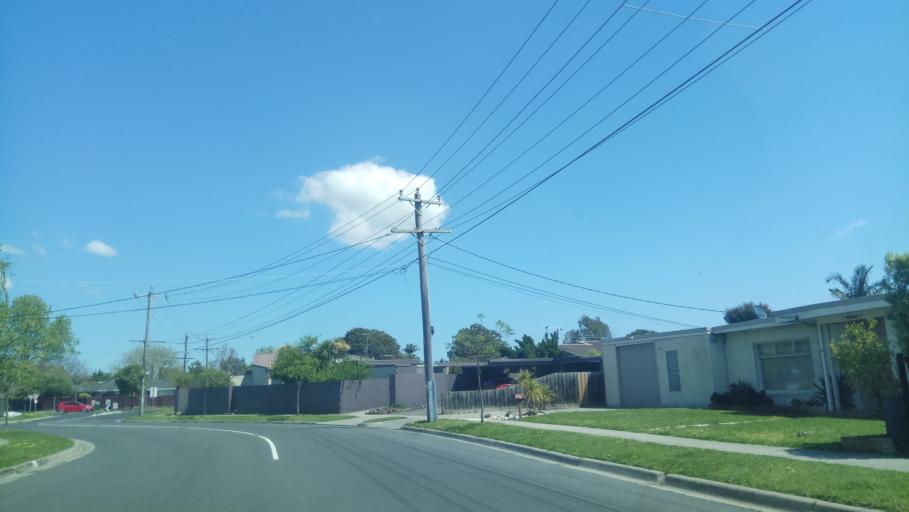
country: AU
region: Victoria
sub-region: Kingston
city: Dingley Village
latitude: -37.9858
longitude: 145.1380
